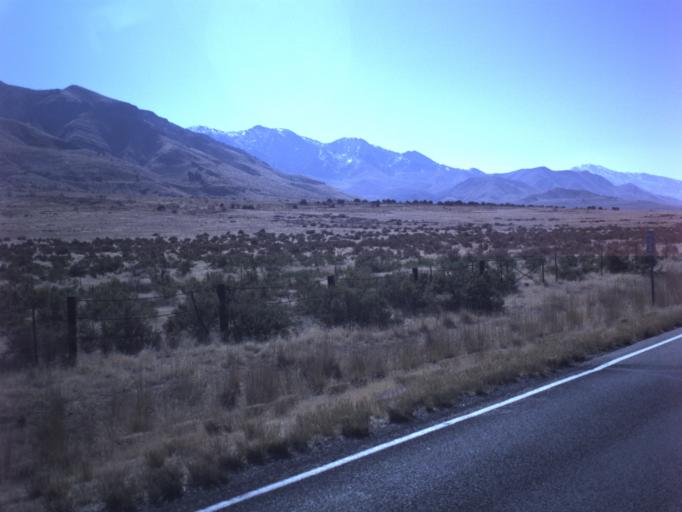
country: US
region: Utah
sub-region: Tooele County
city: Grantsville
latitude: 40.6771
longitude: -112.6722
